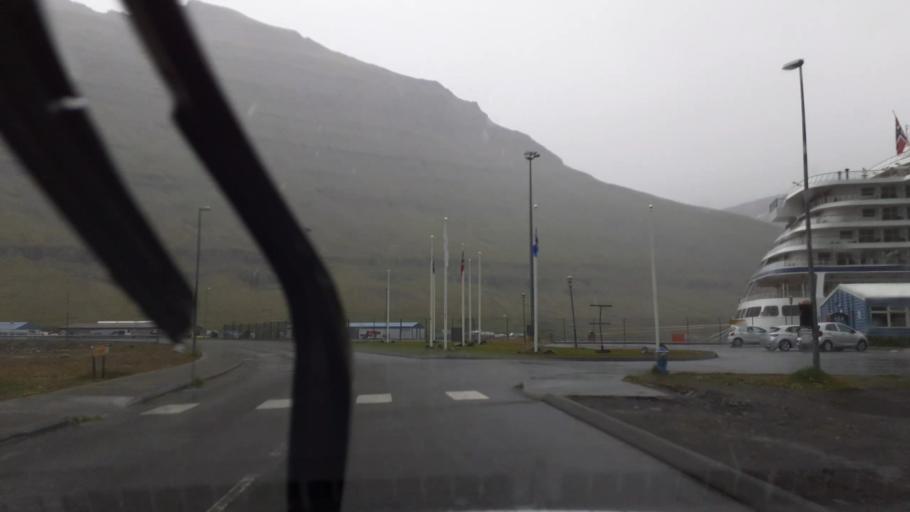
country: IS
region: East
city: Eskifjoerdur
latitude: 65.2626
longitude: -14.0021
